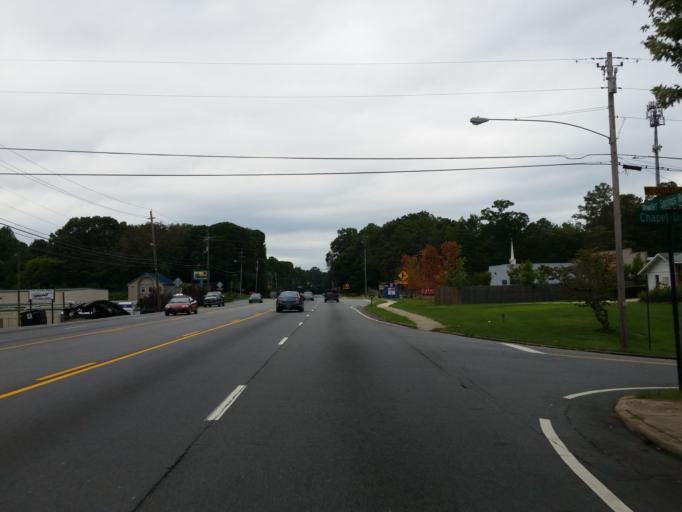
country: US
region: Georgia
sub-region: Cobb County
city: Fair Oaks
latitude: 33.9213
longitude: -84.5793
